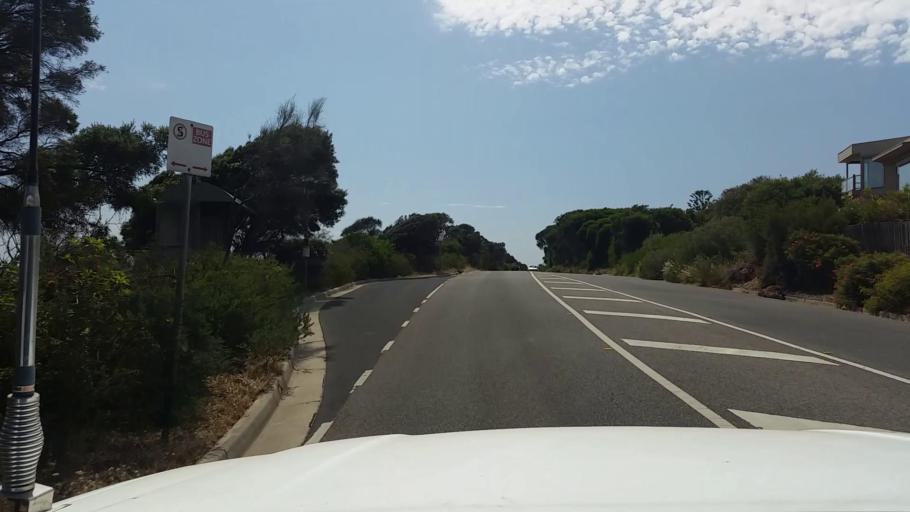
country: AU
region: Victoria
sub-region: Mornington Peninsula
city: Mount Martha
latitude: -38.2620
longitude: 145.0183
